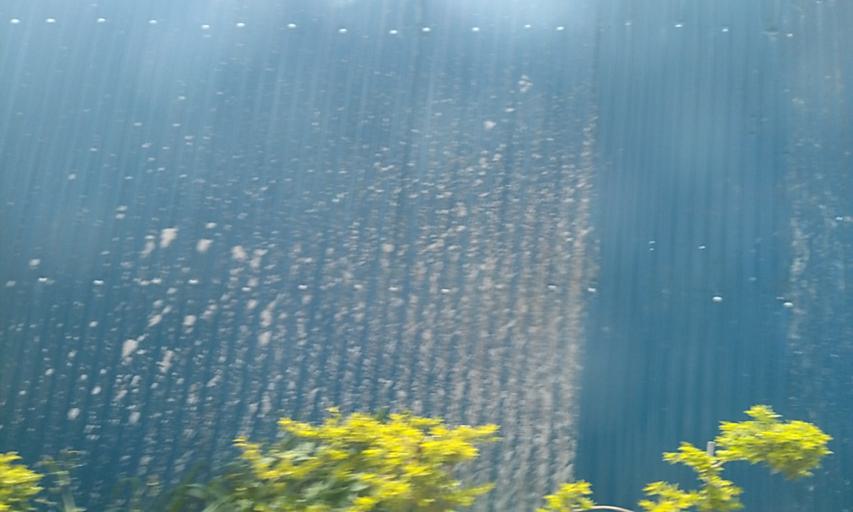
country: UG
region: Central Region
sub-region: Kampala District
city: Kampala
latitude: 0.3289
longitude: 32.6015
